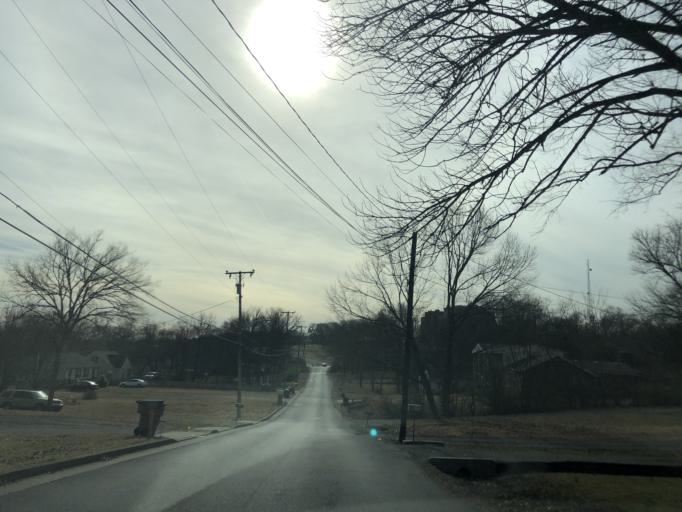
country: US
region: Tennessee
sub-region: Davidson County
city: Nashville
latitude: 36.2193
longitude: -86.7389
